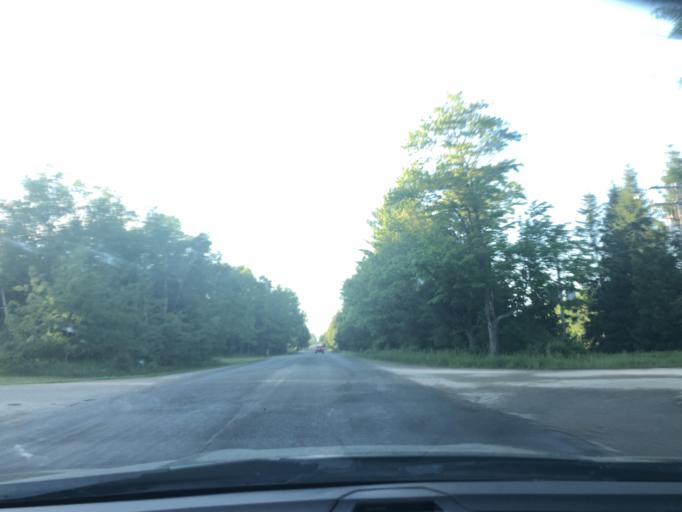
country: US
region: Michigan
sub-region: Missaukee County
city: Lake City
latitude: 44.3872
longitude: -85.0758
